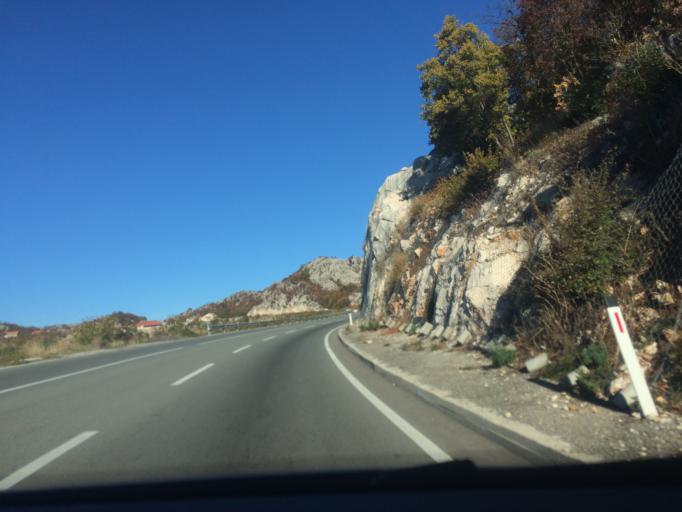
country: ME
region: Cetinje
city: Cetinje
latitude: 42.3824
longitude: 18.9485
